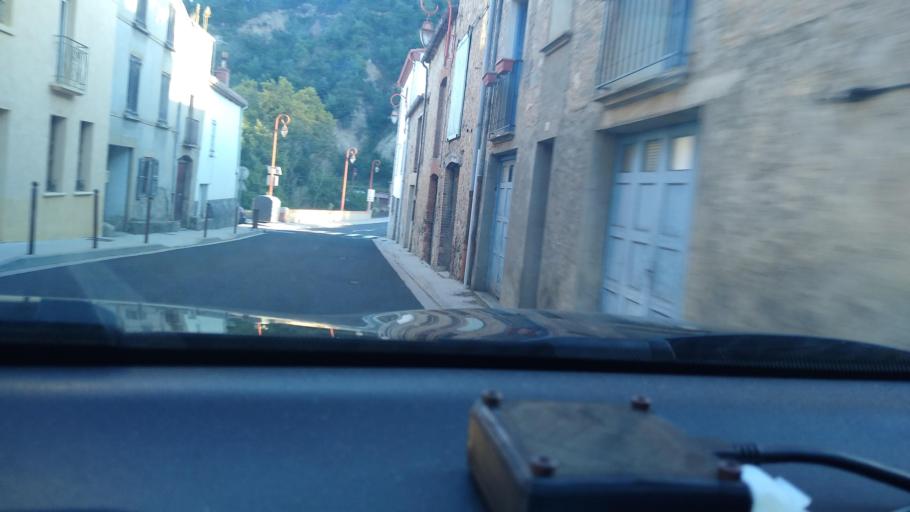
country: FR
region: Languedoc-Roussillon
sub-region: Departement des Pyrenees-Orientales
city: Prades
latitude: 42.6333
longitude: 2.4218
